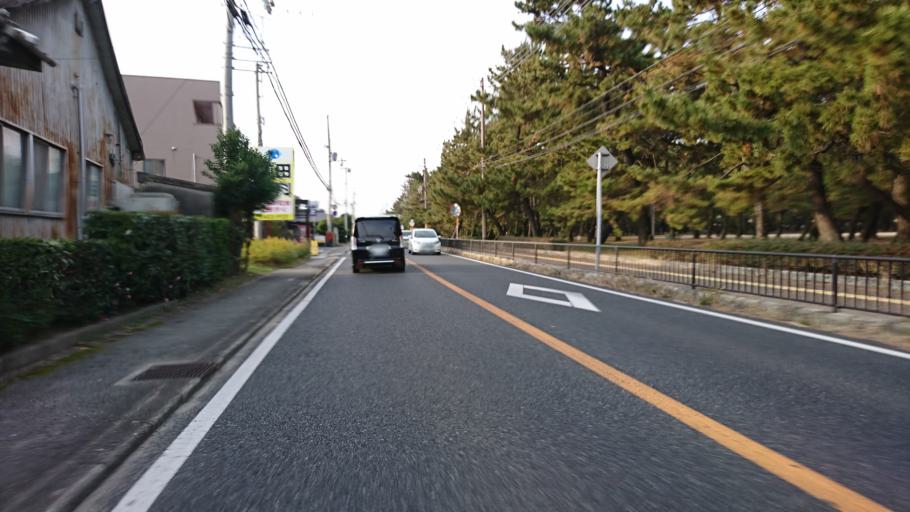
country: JP
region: Hyogo
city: Kakogawacho-honmachi
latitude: 34.7335
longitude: 134.8324
